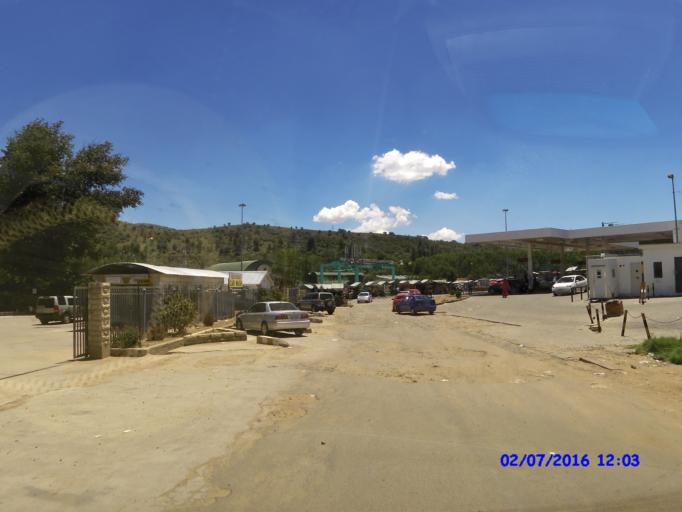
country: LS
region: Maseru
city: Maseru
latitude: -29.3004
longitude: 27.4568
